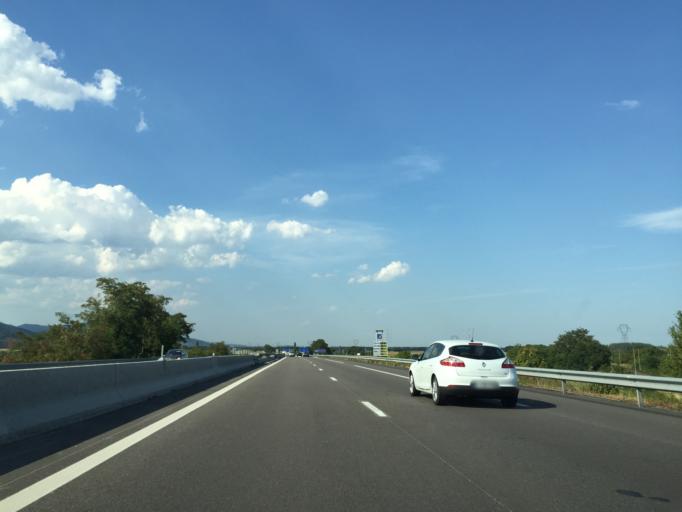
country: FR
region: Alsace
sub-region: Departement du Bas-Rhin
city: Kintzheim
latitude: 48.2242
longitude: 7.4051
